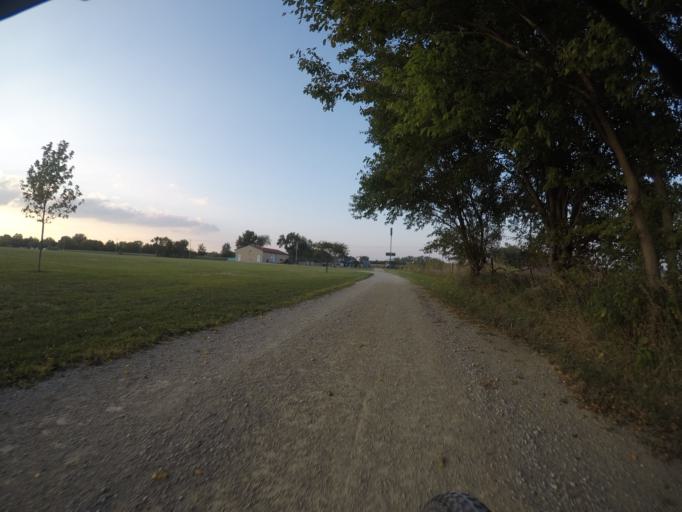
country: US
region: Kansas
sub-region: Riley County
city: Manhattan
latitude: 39.2027
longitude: -96.5445
